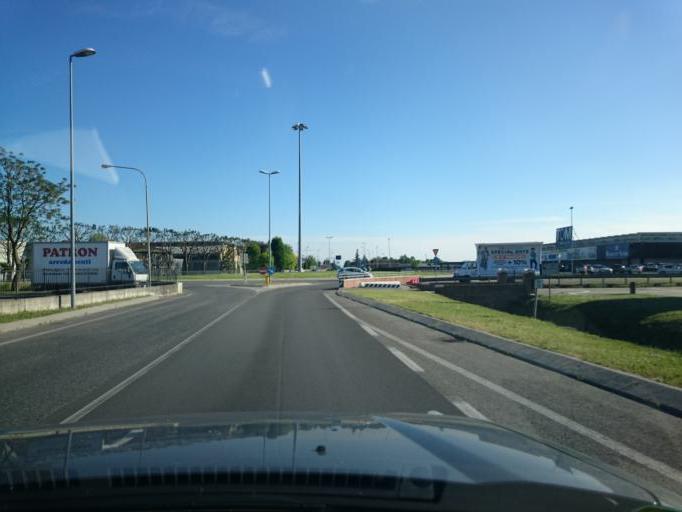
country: IT
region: Veneto
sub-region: Provincia di Venezia
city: Caselle
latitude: 45.4844
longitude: 12.0036
